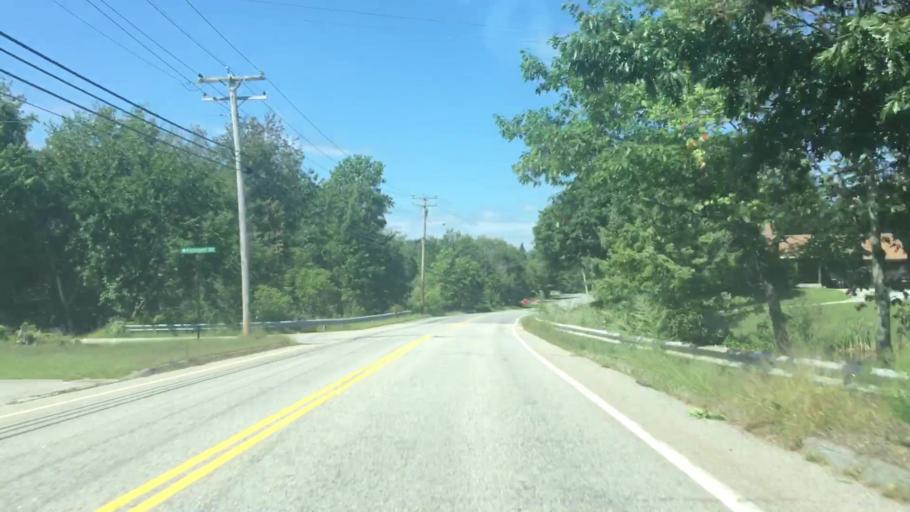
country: US
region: Maine
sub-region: Androscoggin County
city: Sabattus
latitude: 44.0899
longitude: -70.1461
